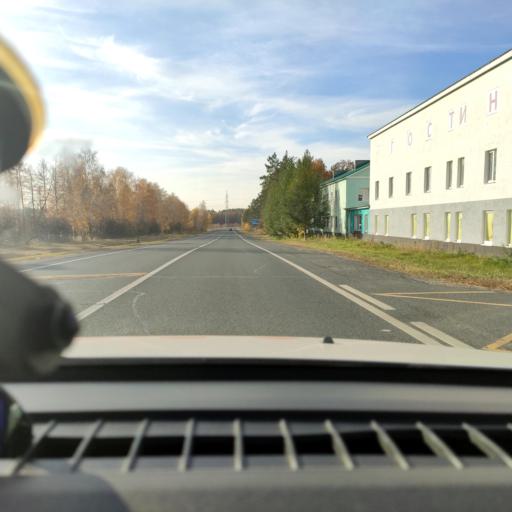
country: RU
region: Samara
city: Volzhskiy
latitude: 53.4554
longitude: 50.1264
